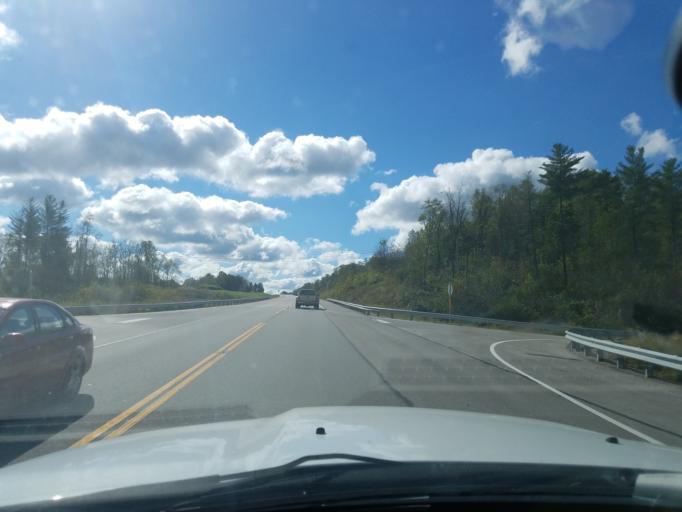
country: US
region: Kentucky
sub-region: Rockcastle County
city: Brodhead
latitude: 37.3766
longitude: -84.4139
